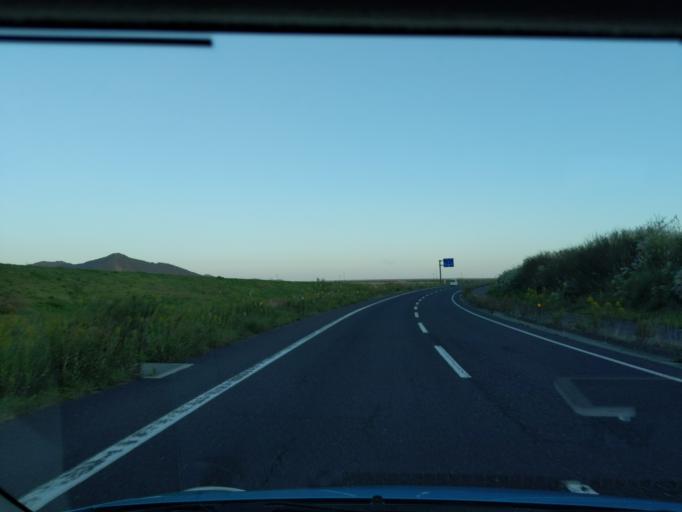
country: JP
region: Iwate
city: Ichinoseki
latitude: 38.9943
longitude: 141.1203
